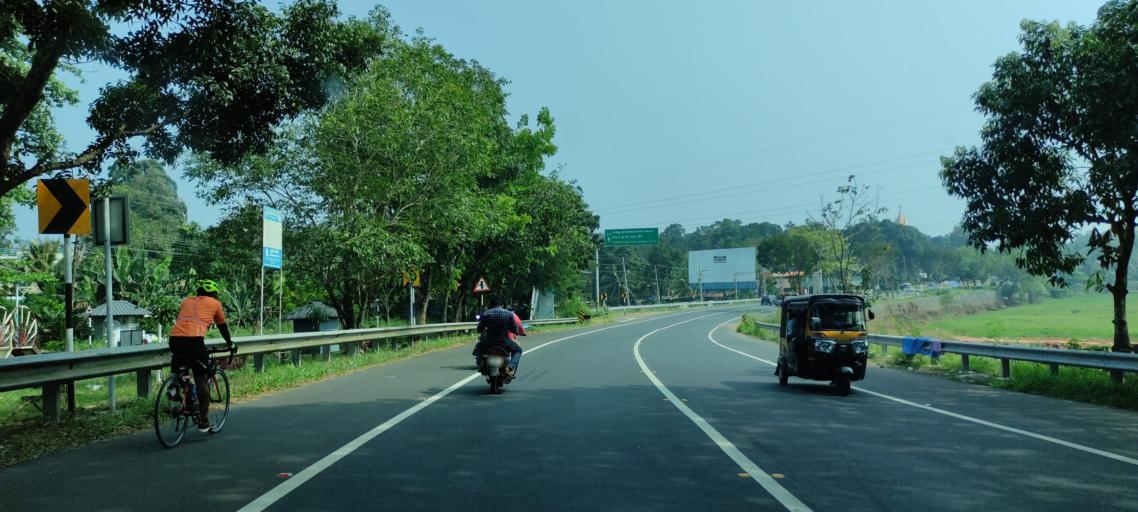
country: IN
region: Kerala
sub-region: Alappuzha
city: Chengannur
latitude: 9.2496
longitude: 76.6670
